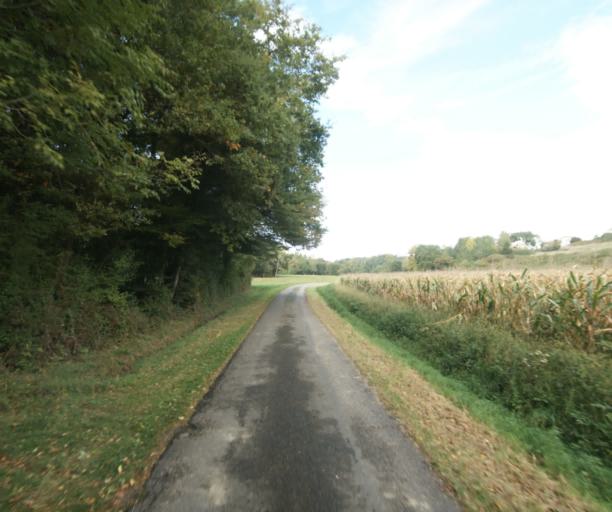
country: FR
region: Aquitaine
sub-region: Departement des Landes
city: Villeneuve-de-Marsan
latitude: 43.9037
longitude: -0.2180
